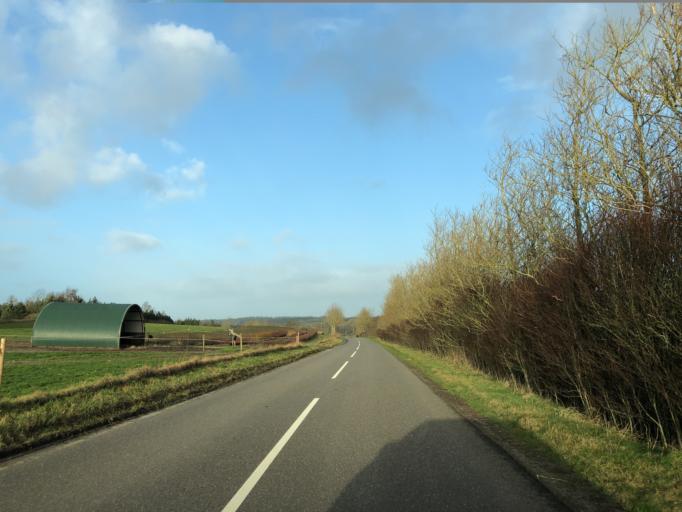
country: DK
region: Central Jutland
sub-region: Ringkobing-Skjern Kommune
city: Videbaek
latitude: 56.1911
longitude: 8.5420
